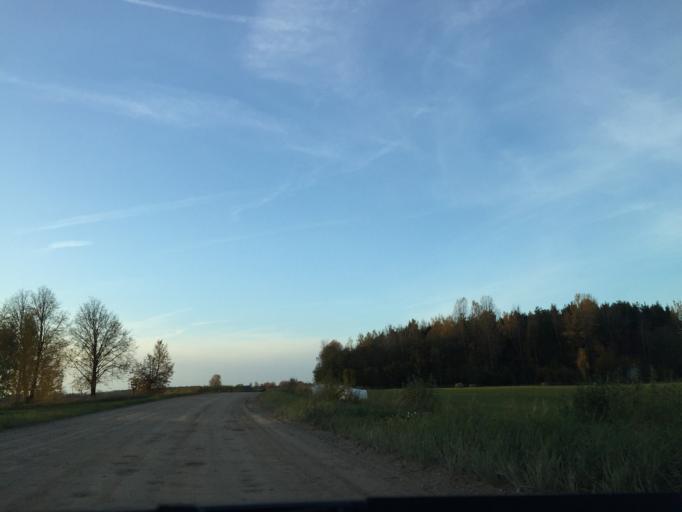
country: LV
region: Malpils
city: Malpils
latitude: 56.8864
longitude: 24.9548
